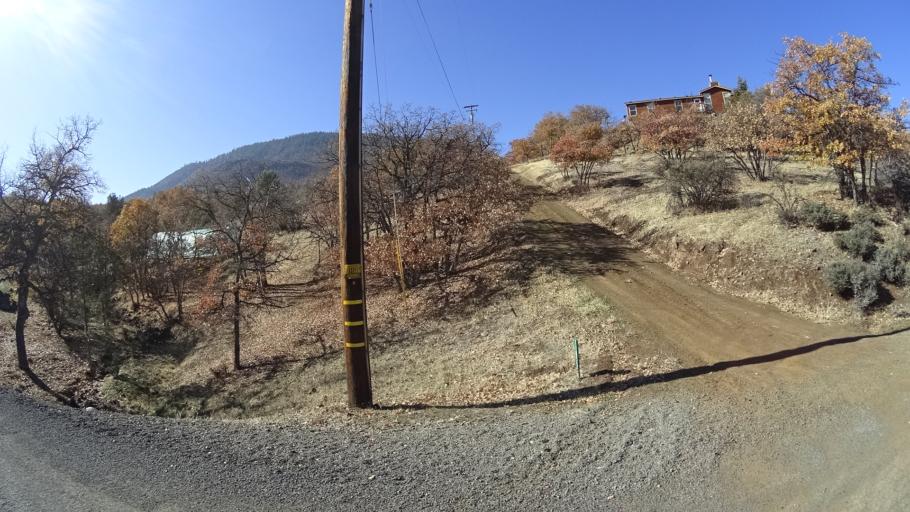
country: US
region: California
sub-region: Siskiyou County
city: Montague
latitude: 41.8742
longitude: -122.4842
